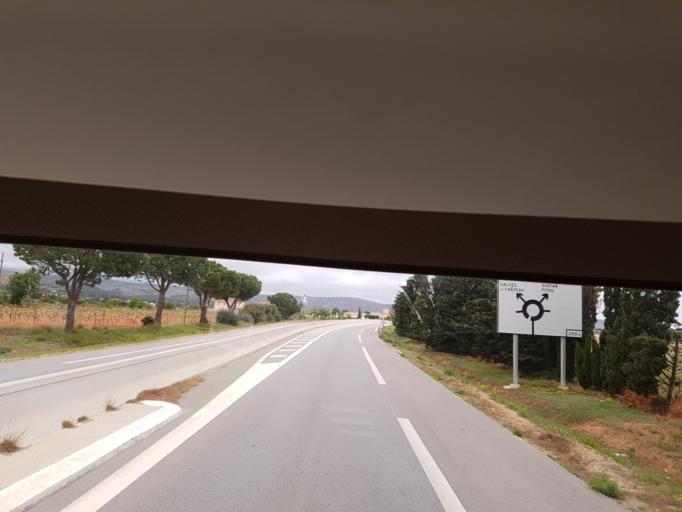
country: FR
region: Languedoc-Roussillon
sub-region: Departement des Pyrenees-Orientales
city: Salses-le-Chateau
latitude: 42.8209
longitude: 2.9162
